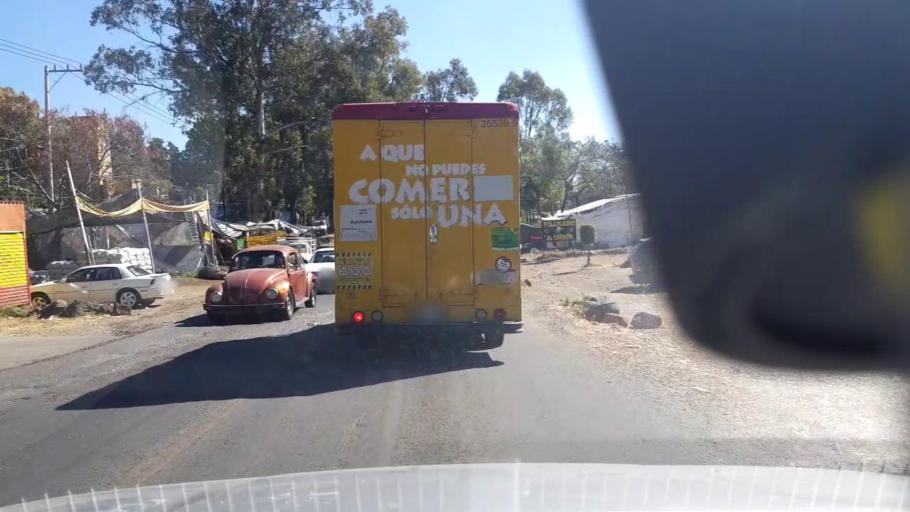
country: MX
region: Morelos
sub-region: Cuernavaca
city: Lomas de Ahuatepec
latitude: 18.9696
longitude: -99.2148
